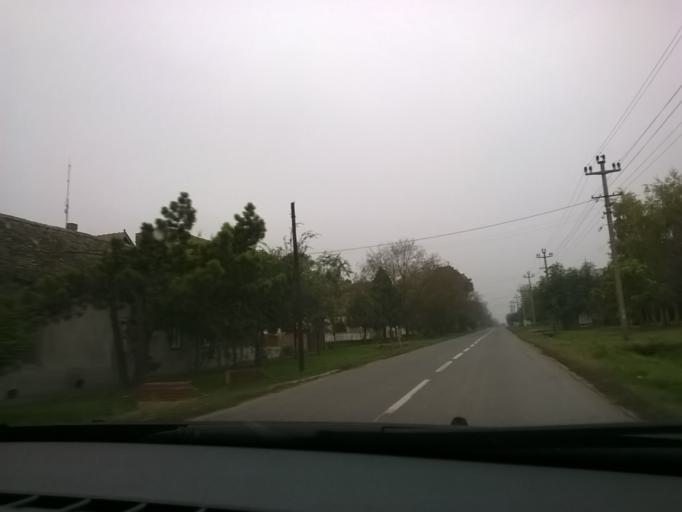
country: RS
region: Autonomna Pokrajina Vojvodina
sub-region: Juznobanatski Okrug
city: Kovin
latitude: 44.8827
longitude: 20.9671
